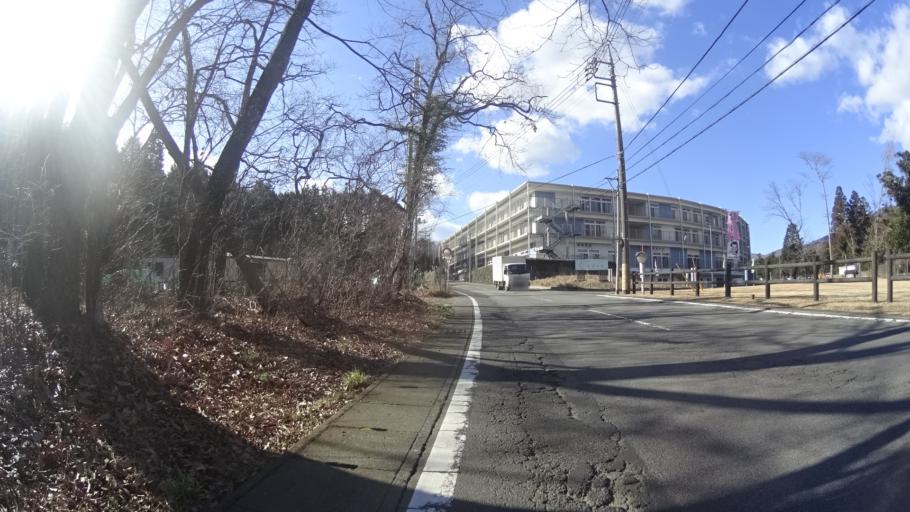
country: JP
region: Shizuoka
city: Gotemba
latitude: 35.3443
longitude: 138.8985
